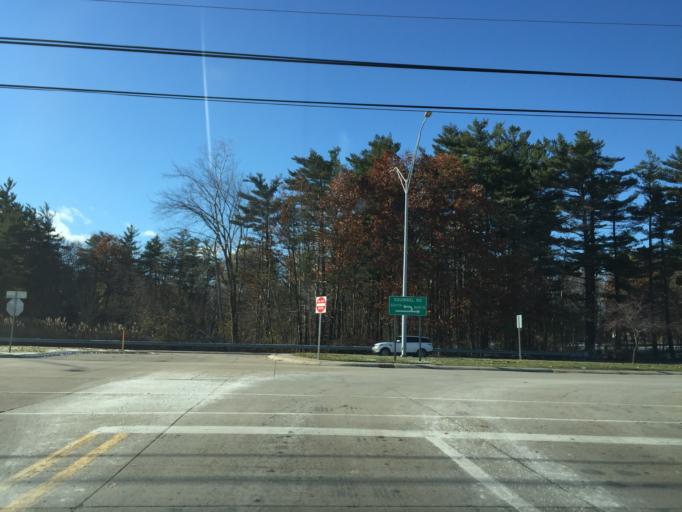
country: US
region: Michigan
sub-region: Oakland County
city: Auburn Hills
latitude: 42.6686
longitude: -83.2198
